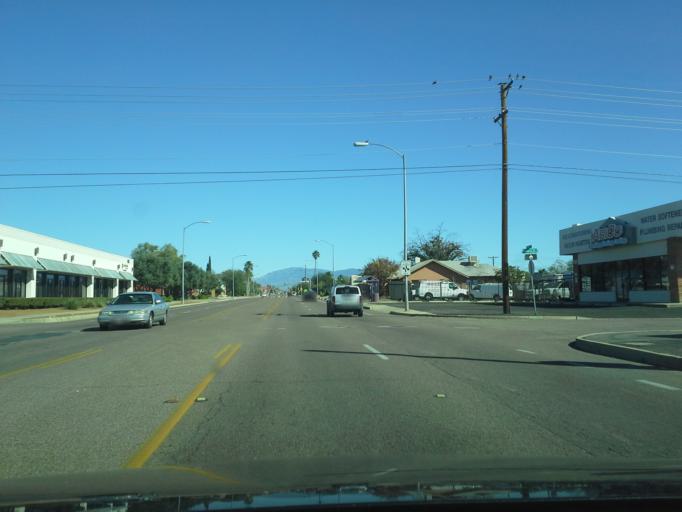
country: US
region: Arizona
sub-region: Pima County
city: South Tucson
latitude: 32.2213
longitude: -110.9551
